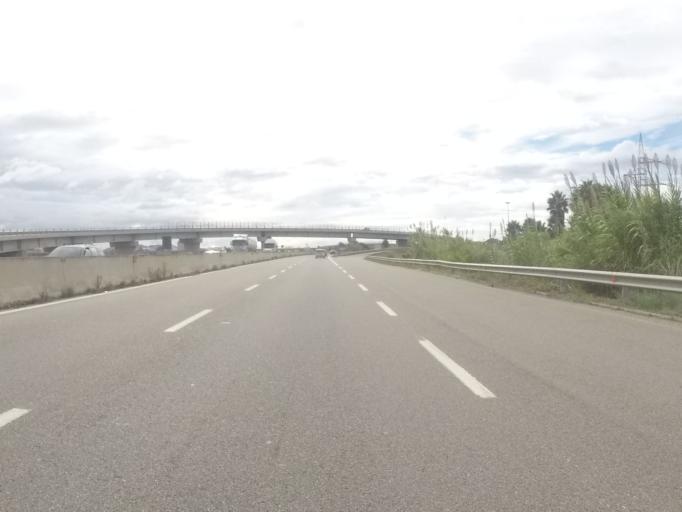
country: IT
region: Sardinia
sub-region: Provincia di Cagliari
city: Cagliari
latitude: 39.2213
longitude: 9.0830
